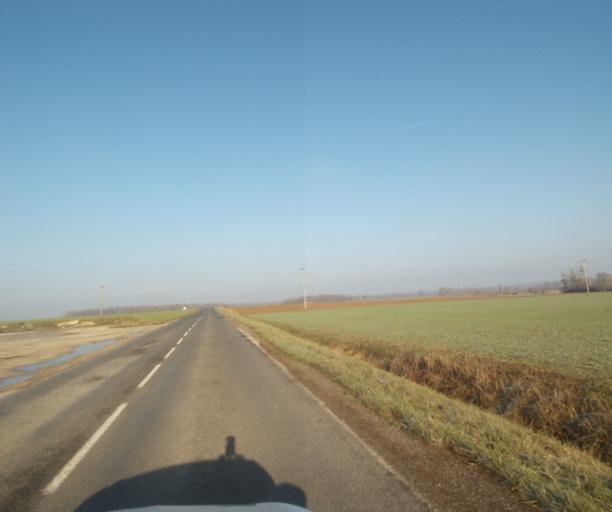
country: FR
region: Champagne-Ardenne
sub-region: Departement de la Haute-Marne
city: Montier-en-Der
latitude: 48.4957
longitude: 4.7540
